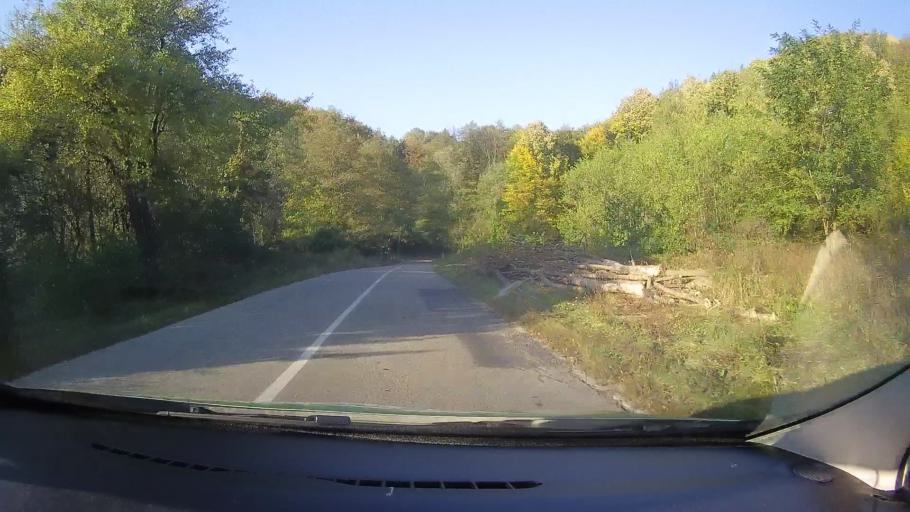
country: RO
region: Timis
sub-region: Comuna Nadrag
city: Nadrag
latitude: 45.6688
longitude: 22.1651
